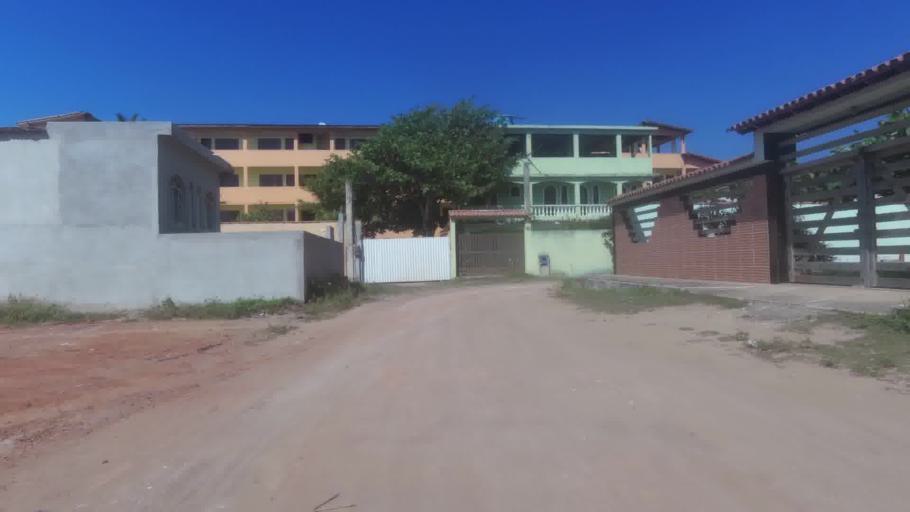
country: BR
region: Espirito Santo
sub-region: Marataizes
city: Marataizes
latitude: -21.0694
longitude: -40.8371
